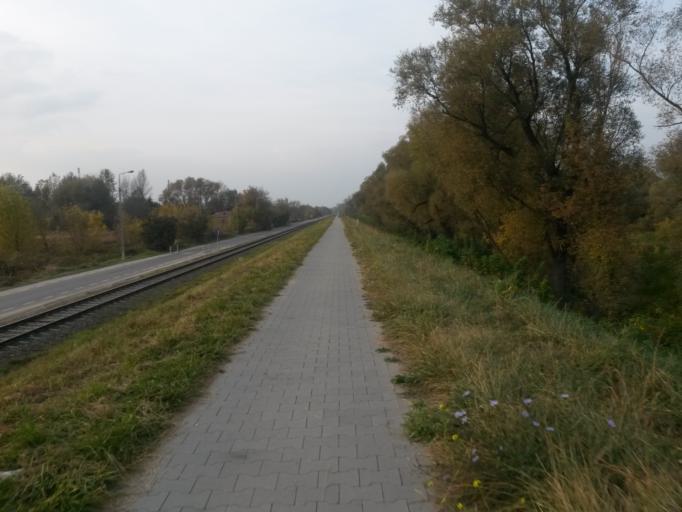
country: PL
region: Masovian Voivodeship
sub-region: Warszawa
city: Wilanow
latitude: 52.1746
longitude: 21.1191
